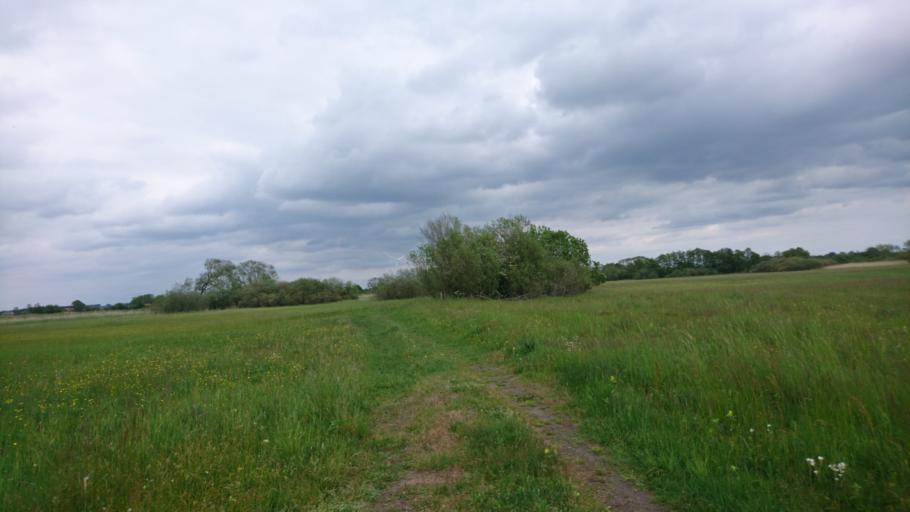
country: SE
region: Skane
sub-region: Kristianstads Kommun
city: Fjalkinge
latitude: 56.0027
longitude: 14.2447
